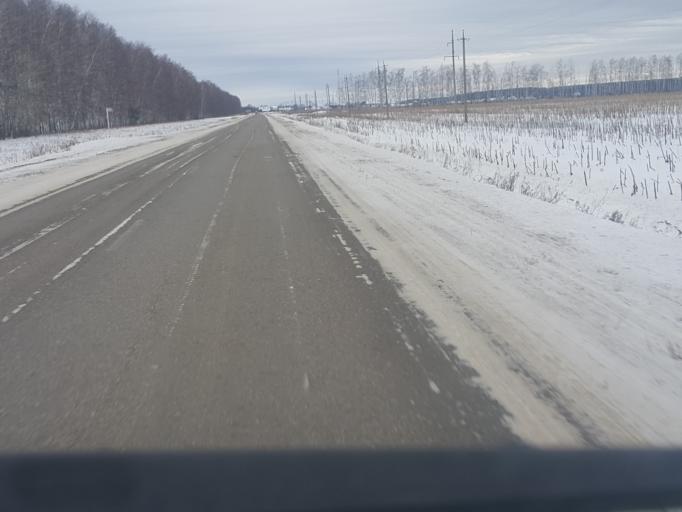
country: RU
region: Tambov
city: Rasskazovo
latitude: 52.8159
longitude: 41.7949
